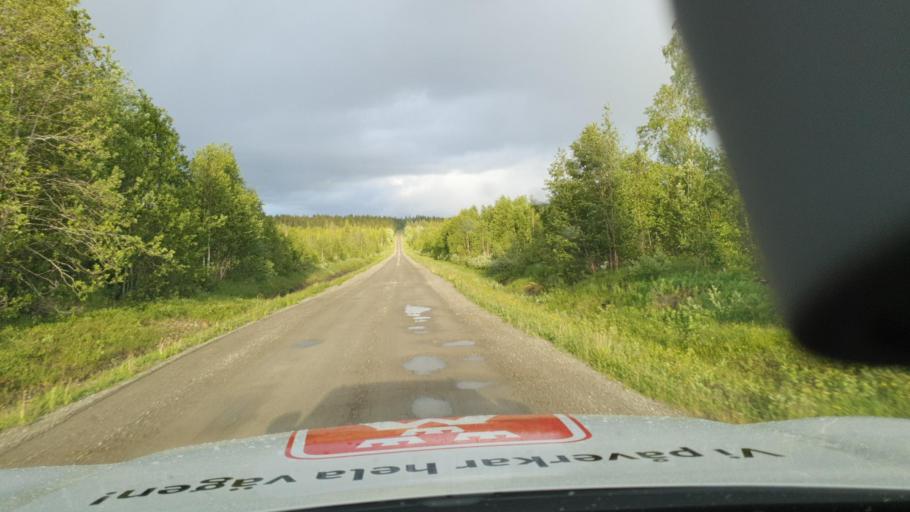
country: SE
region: Vaesterbotten
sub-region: Storumans Kommun
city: Storuman
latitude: 64.7906
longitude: 17.0089
